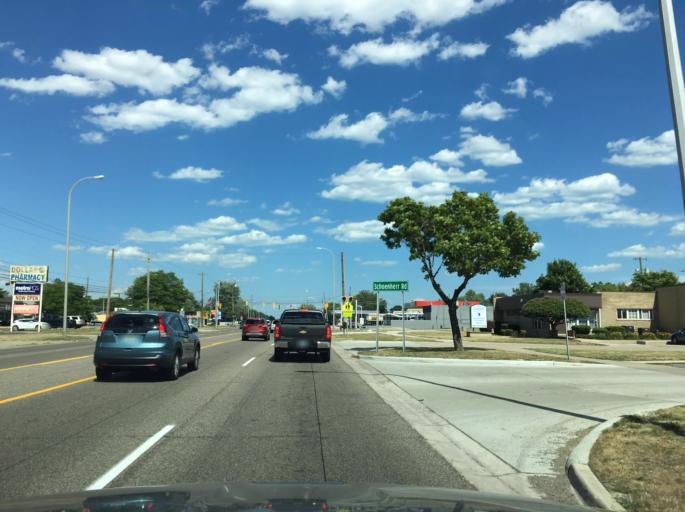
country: US
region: Michigan
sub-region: Macomb County
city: Center Line
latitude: 42.5076
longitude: -82.9892
